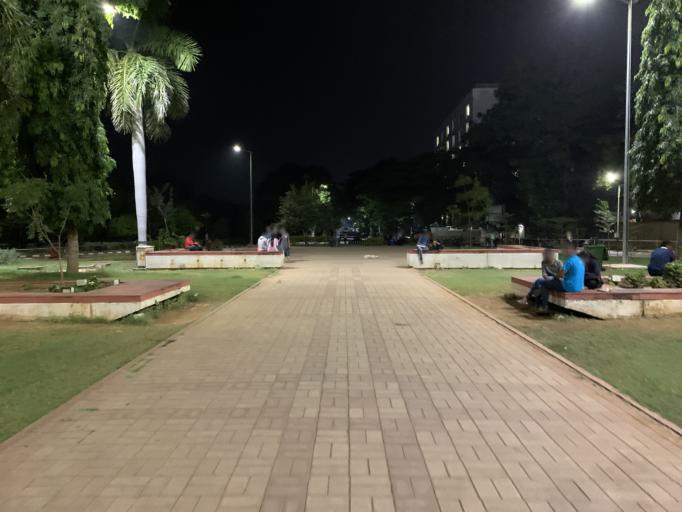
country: IN
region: Telangana
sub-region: Warangal
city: Warangal
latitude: 17.9850
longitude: 79.5308
